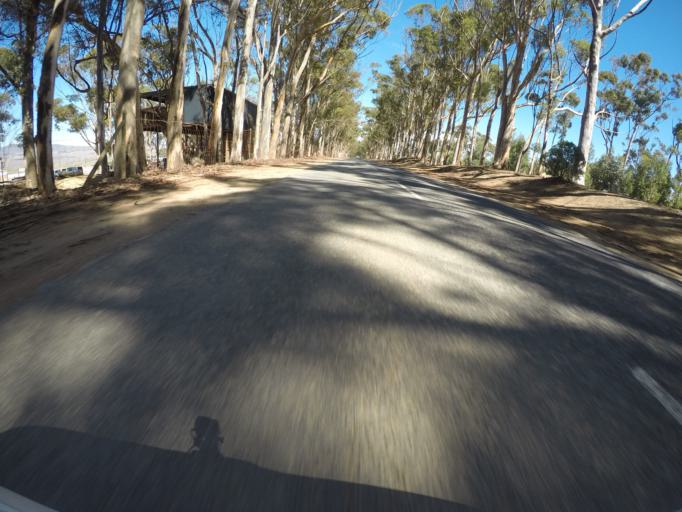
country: ZA
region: Western Cape
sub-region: City of Cape Town
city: Sunset Beach
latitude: -33.7618
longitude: 18.5523
